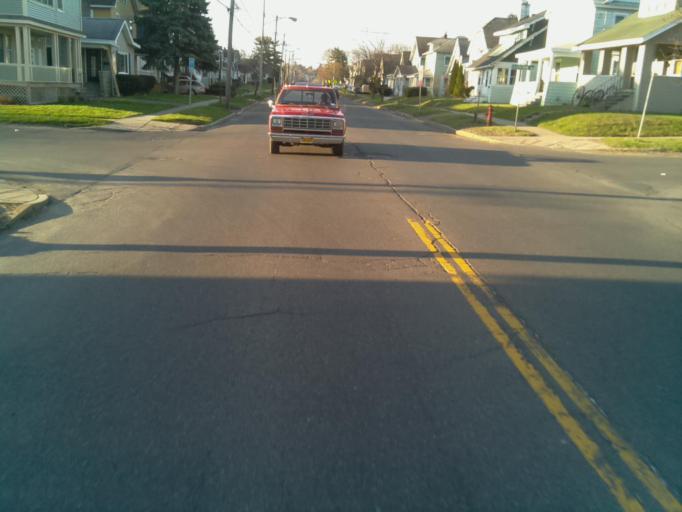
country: US
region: New York
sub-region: Onondaga County
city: East Syracuse
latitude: 43.0641
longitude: -76.1045
